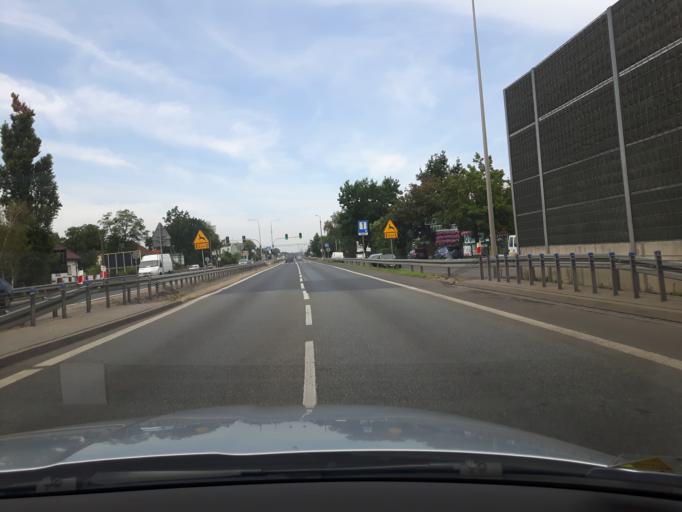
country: PL
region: Masovian Voivodeship
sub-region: Powiat warszawski zachodni
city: Lomianki
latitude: 52.3306
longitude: 20.8954
